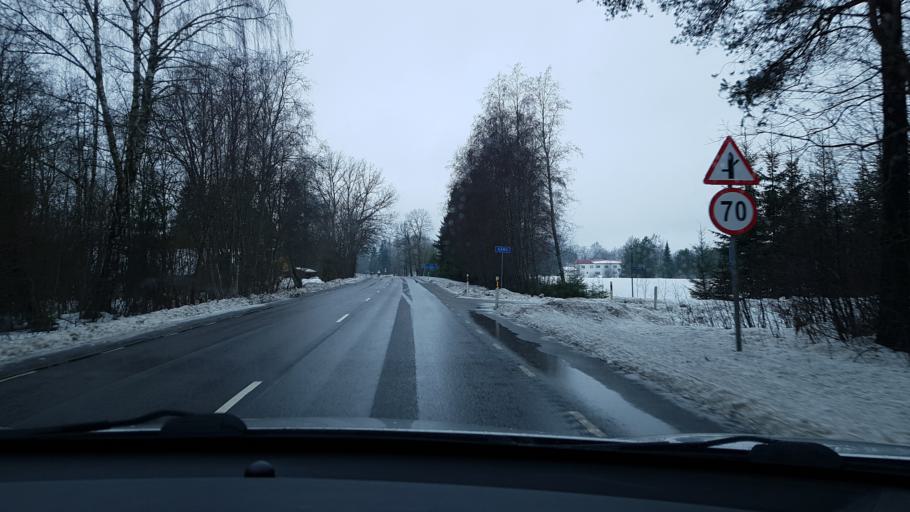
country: EE
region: Paernumaa
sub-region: Vaendra vald (alev)
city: Vandra
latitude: 58.8204
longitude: 25.1486
